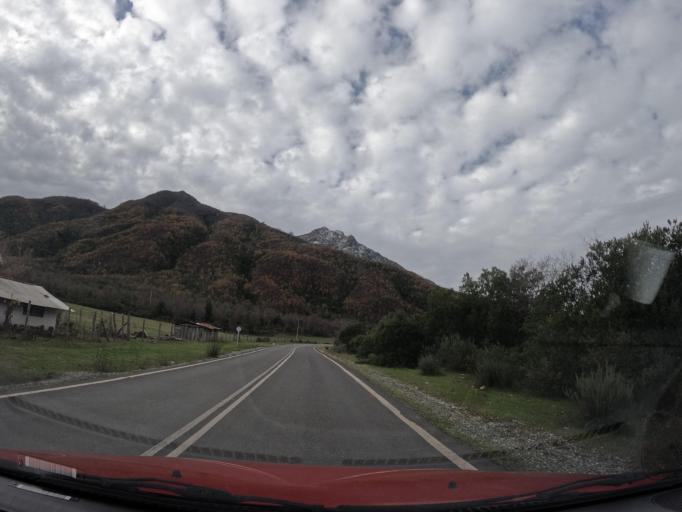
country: CL
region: Maule
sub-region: Provincia de Linares
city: Colbun
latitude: -35.8589
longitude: -71.2475
